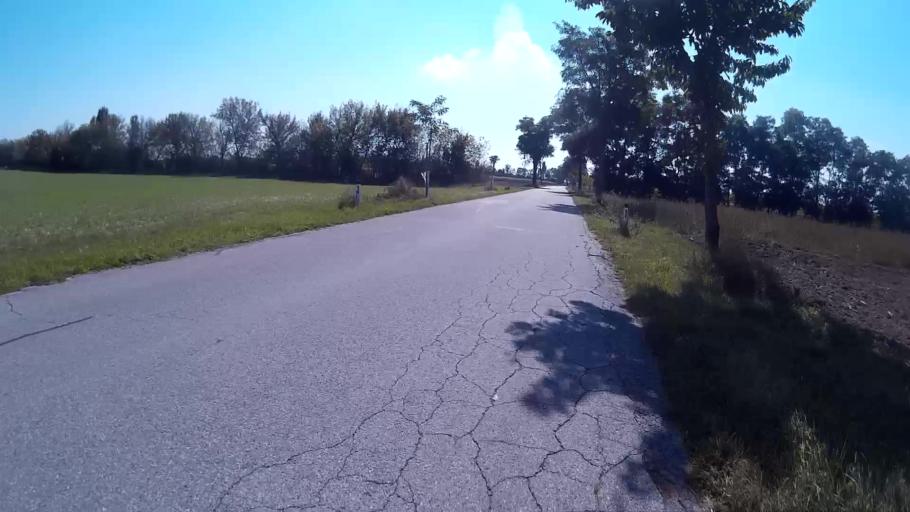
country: CZ
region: South Moravian
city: Novosedly
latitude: 48.7862
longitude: 16.4911
